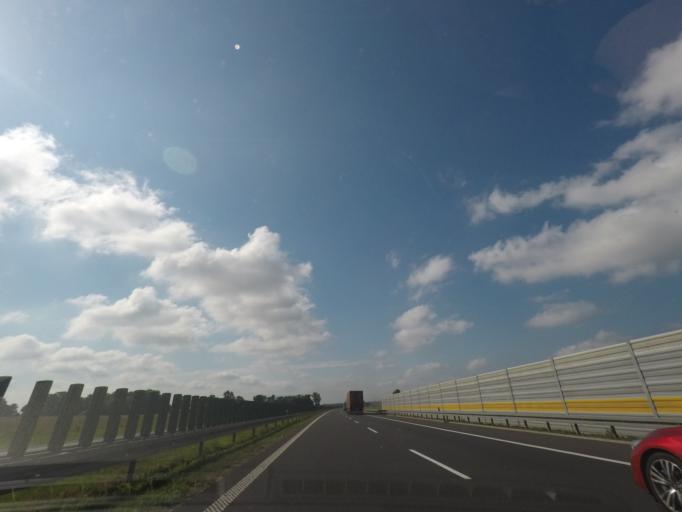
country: PL
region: Pomeranian Voivodeship
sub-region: Powiat starogardzki
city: Smetowo Graniczne
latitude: 53.7146
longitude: 18.6298
